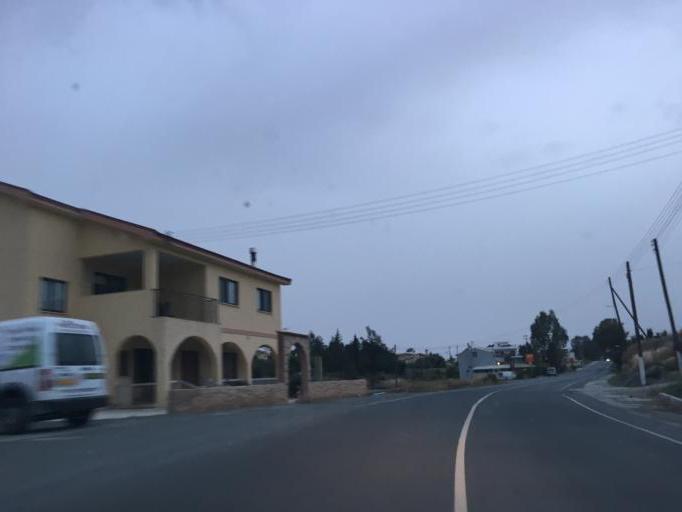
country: CY
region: Limassol
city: Parekklisha
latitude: 34.7495
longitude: 33.1614
